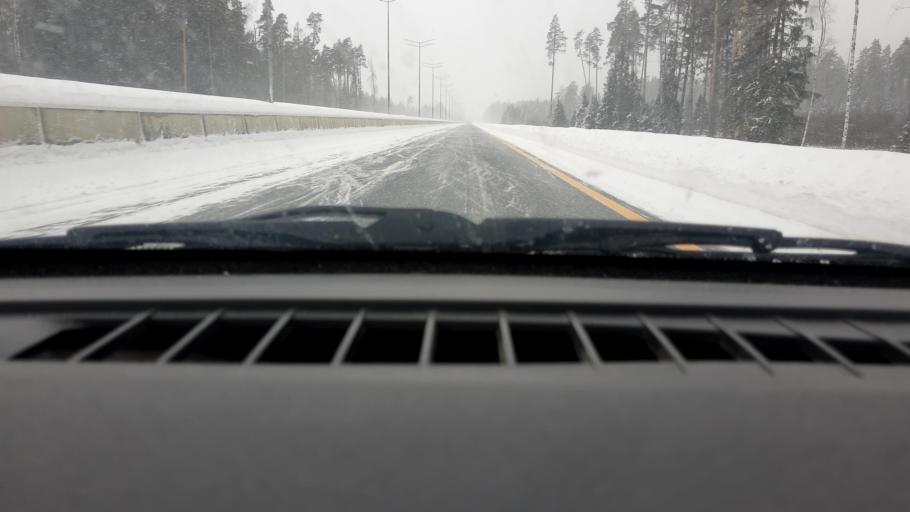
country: RU
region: Moskovskaya
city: Chernogolovka
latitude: 56.0154
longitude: 38.2589
